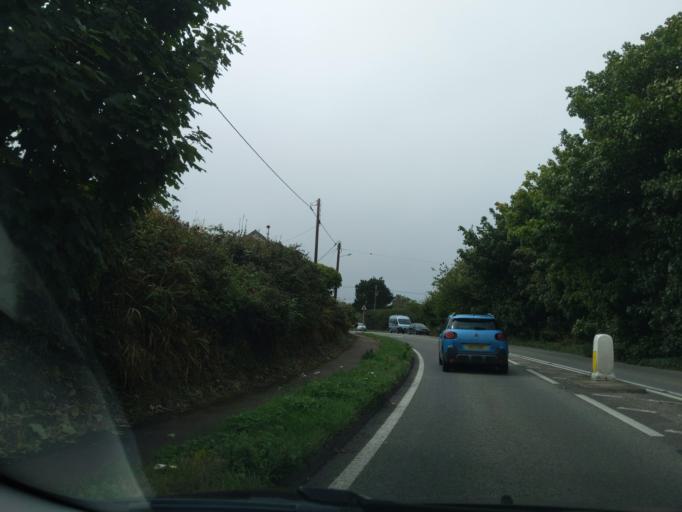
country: GB
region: England
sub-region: Cornwall
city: Porthleven
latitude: 50.1079
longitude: -5.3347
